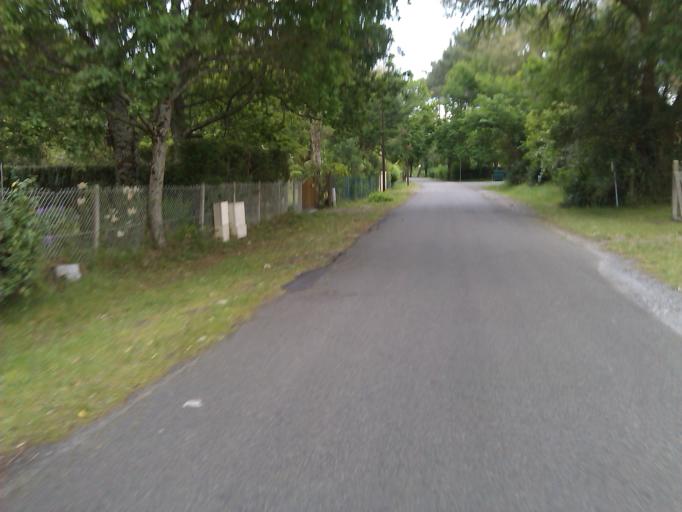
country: FR
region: Aquitaine
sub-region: Departement des Landes
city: Leon
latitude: 43.8480
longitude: -1.3556
